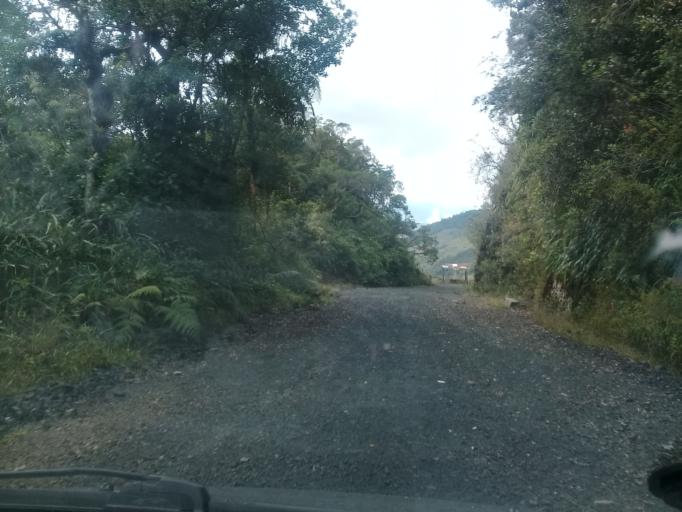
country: CO
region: Cundinamarca
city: Gachala
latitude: 4.7021
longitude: -73.4275
